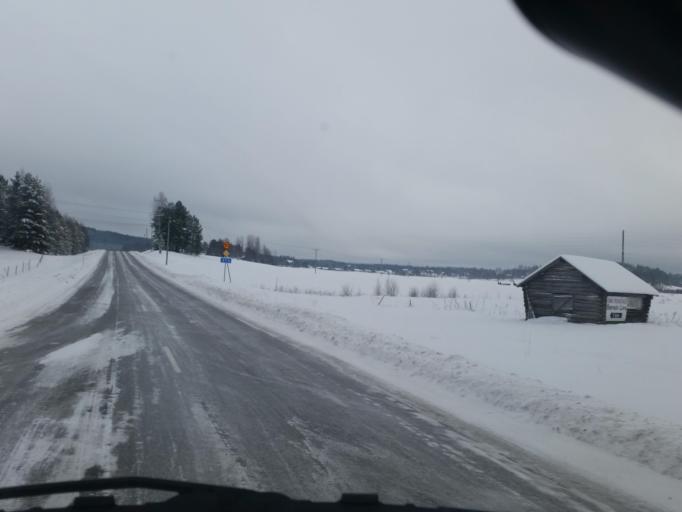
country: SE
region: Norrbotten
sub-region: Pitea Kommun
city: Roknas
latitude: 65.3260
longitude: 21.2212
